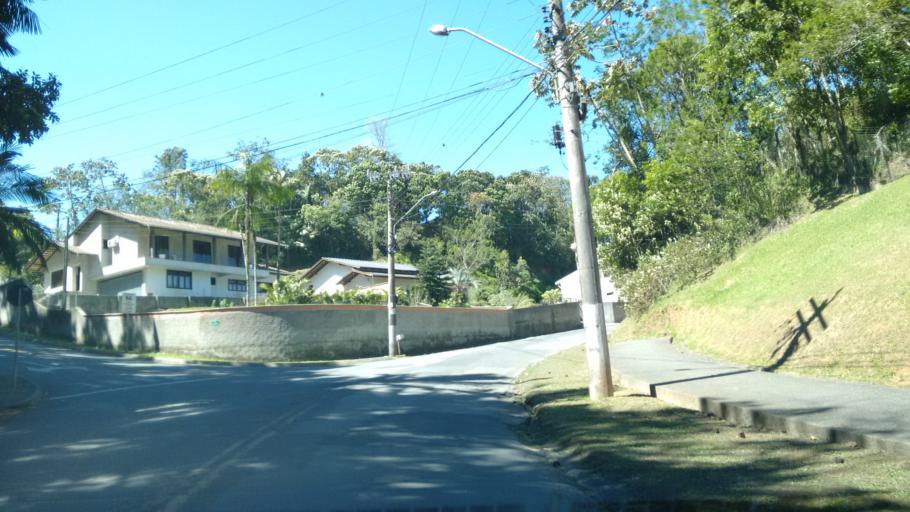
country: BR
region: Santa Catarina
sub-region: Blumenau
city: Blumenau
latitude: -26.8851
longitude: -49.1374
